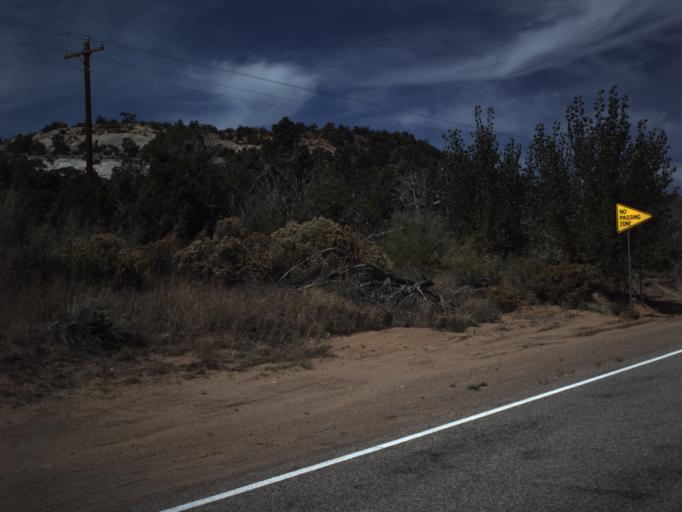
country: US
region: Utah
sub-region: Wayne County
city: Loa
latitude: 37.9163
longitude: -111.4245
